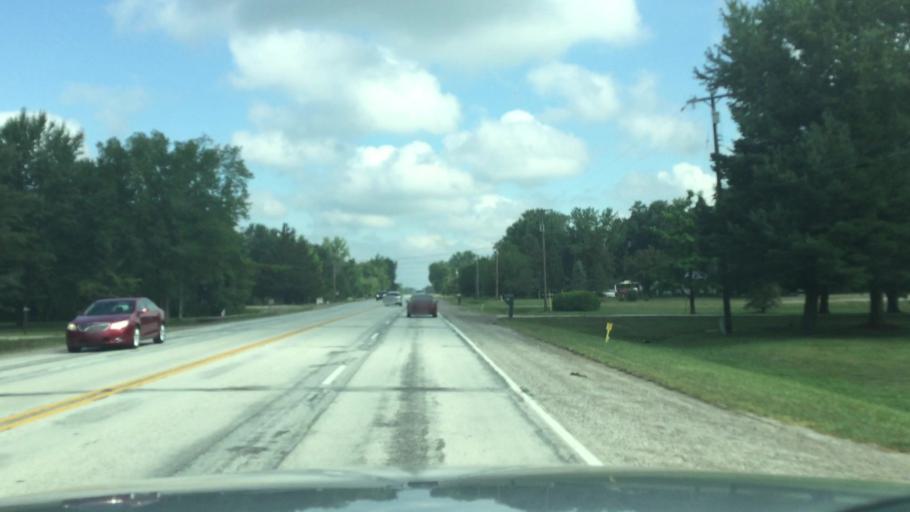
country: US
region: Michigan
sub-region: Genesee County
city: Clio
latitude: 43.2243
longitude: -83.7498
